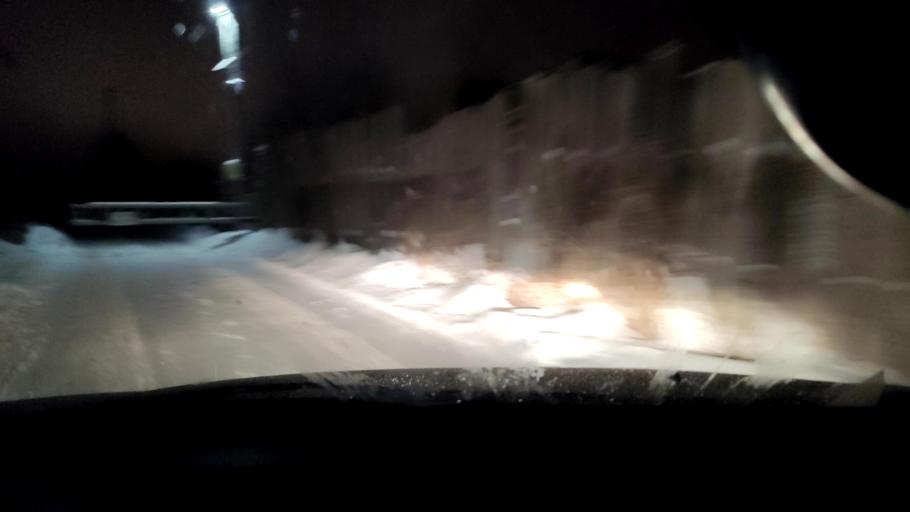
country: RU
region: Perm
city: Kondratovo
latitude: 58.0115
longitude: 56.0321
